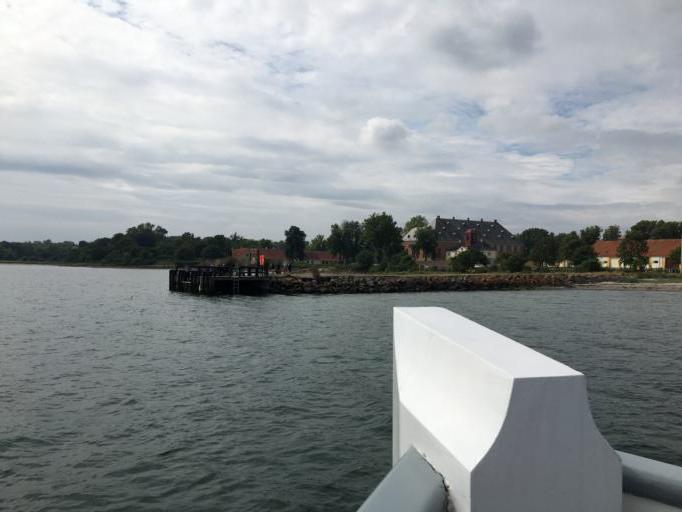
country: DK
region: South Denmark
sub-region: Svendborg Kommune
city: Thuro By
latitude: 55.0206
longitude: 10.6572
